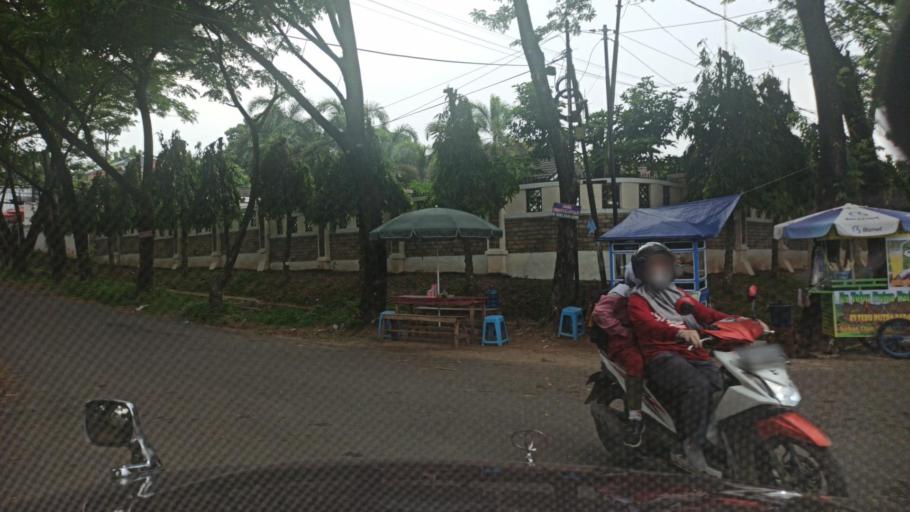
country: ID
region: South Sumatra
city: Plaju
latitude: -2.9932
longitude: 104.7450
